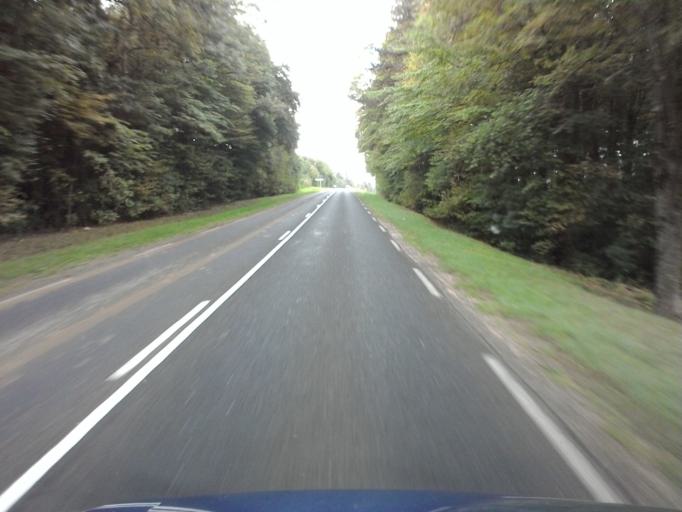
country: FR
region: Lorraine
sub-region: Departement de Meurthe-et-Moselle
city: Colombey-les-Belles
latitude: 48.5015
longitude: 5.8750
